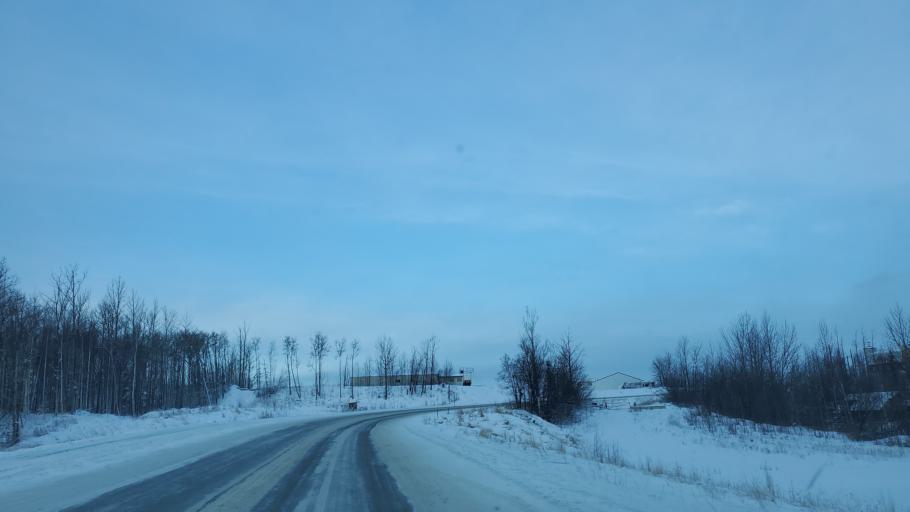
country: US
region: Alaska
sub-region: Matanuska-Susitna Borough
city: Gateway
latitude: 61.5591
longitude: -149.2723
